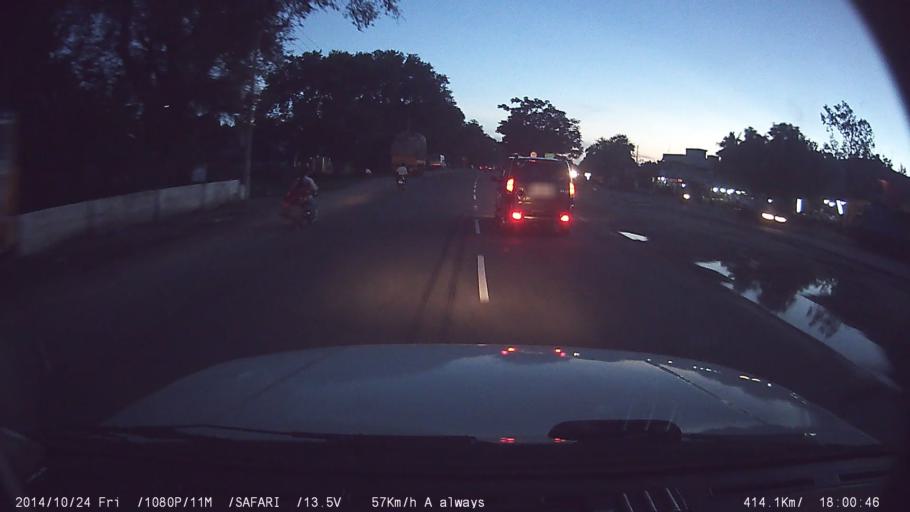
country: IN
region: Tamil Nadu
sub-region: Kancheepuram
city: Chengalpattu
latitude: 12.6480
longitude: 79.9408
